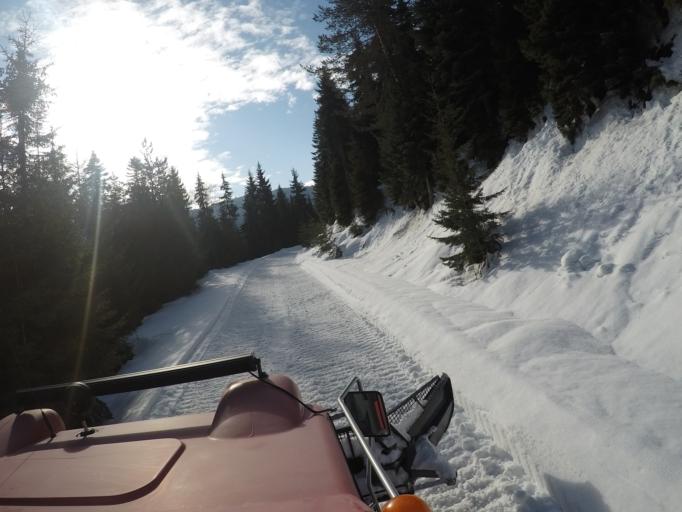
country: GE
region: Samtskhe-Javakheti
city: Adigeni
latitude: 41.6473
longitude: 42.5991
